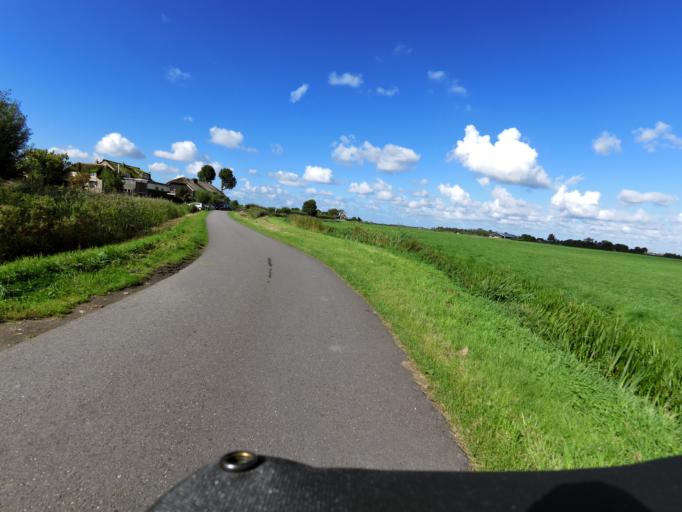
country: NL
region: South Holland
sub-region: Gemeente Vlaardingen
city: Vlaardingen
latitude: 51.9443
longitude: 4.3234
